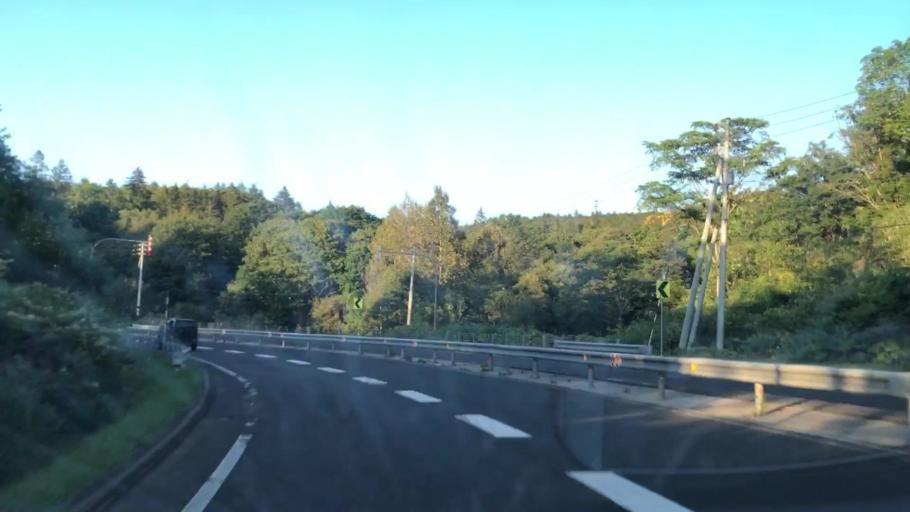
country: JP
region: Hokkaido
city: Otaru
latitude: 42.8454
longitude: 141.0698
